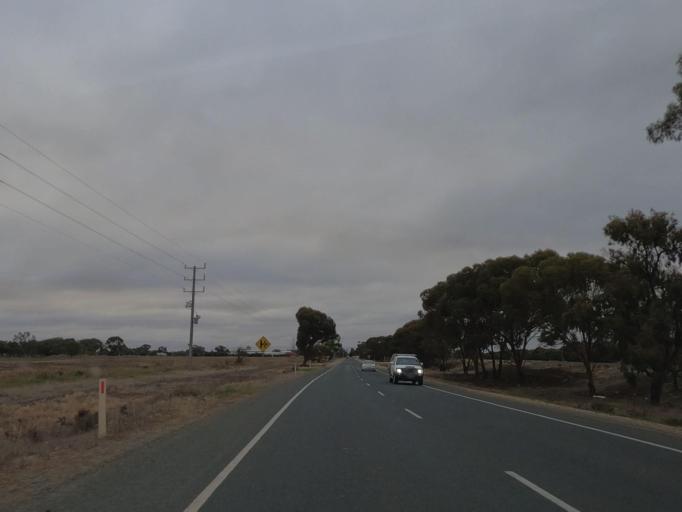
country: AU
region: Victoria
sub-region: Swan Hill
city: Swan Hill
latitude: -35.3946
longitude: 143.5723
